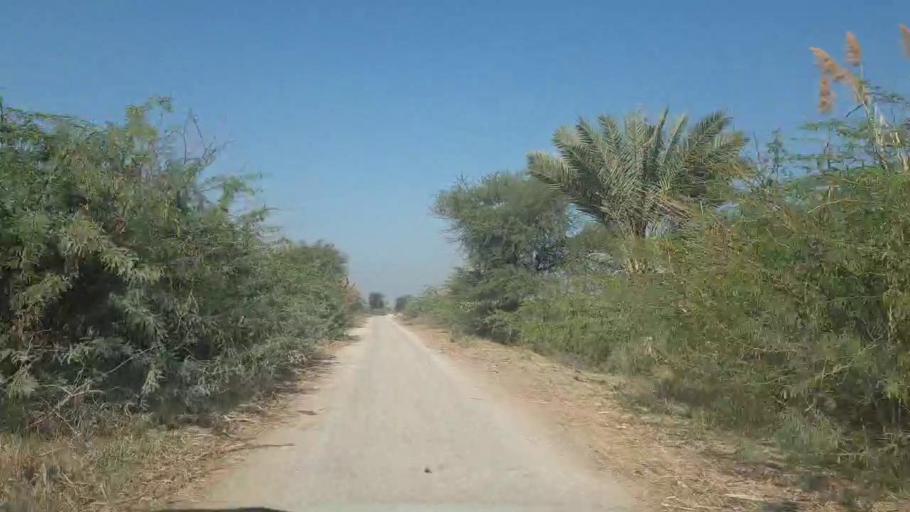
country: PK
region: Sindh
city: Mirpur Khas
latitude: 25.5117
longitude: 69.1711
